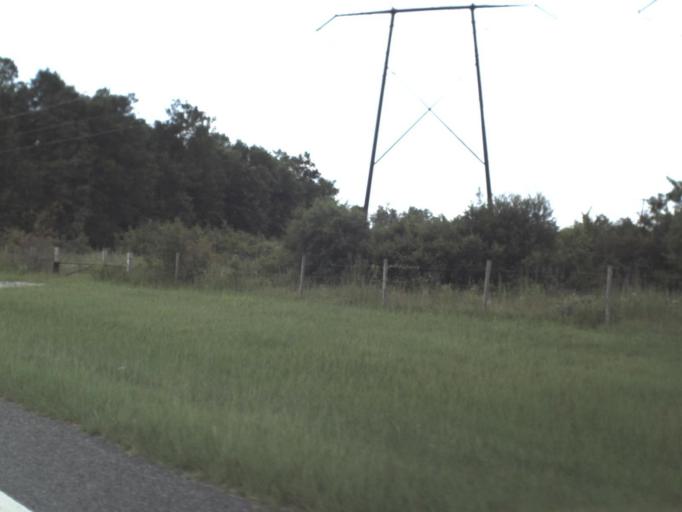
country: US
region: Florida
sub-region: Clay County
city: Asbury Lake
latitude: 29.9778
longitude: -81.8609
